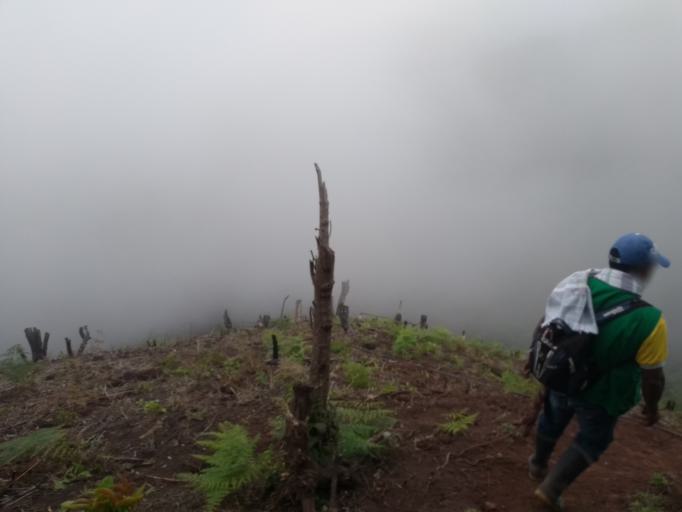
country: CO
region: Cesar
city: Manaure Balcon del Cesar
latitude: 10.1763
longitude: -73.0132
